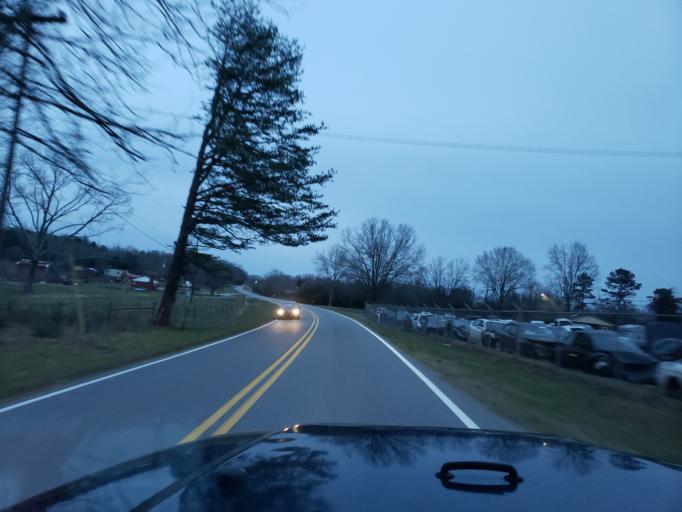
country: US
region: North Carolina
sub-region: Cleveland County
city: White Plains
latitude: 35.2050
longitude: -81.4517
